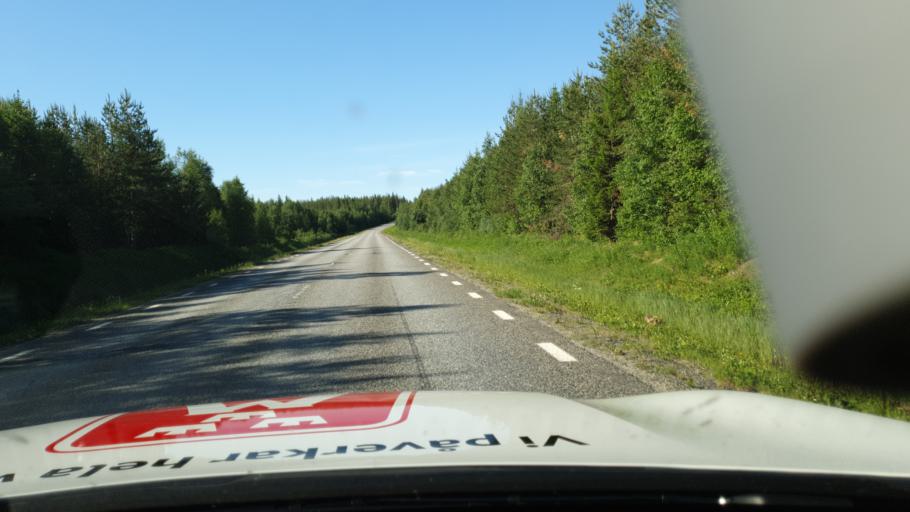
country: SE
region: Vaesterbotten
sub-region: Lycksele Kommun
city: Lycksele
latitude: 64.5242
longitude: 18.4436
